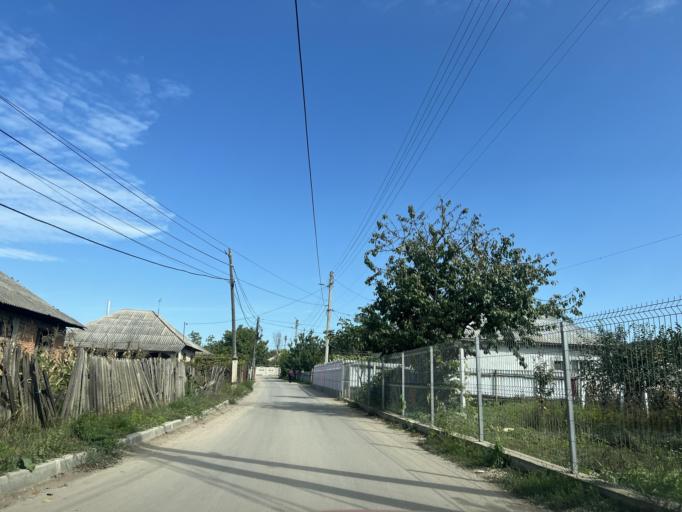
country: MD
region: Ungheni
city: Ungheni
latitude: 47.1996
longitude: 27.8136
